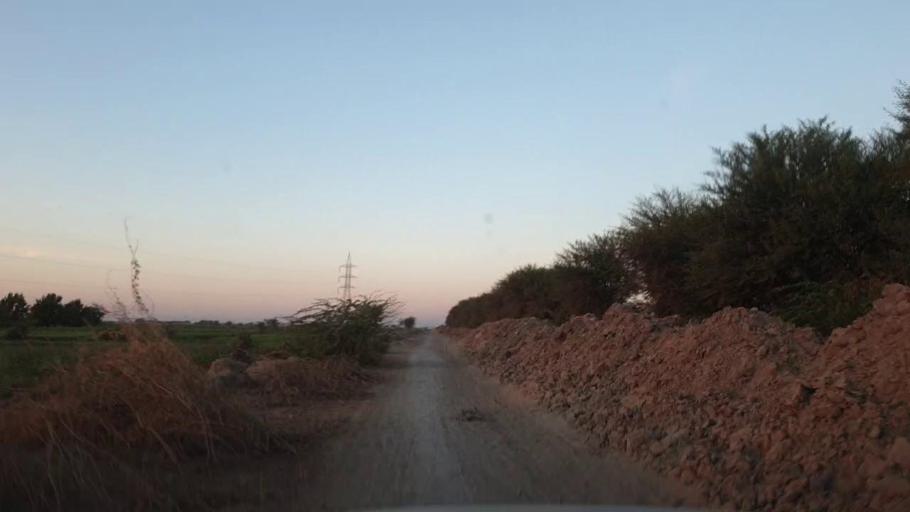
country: PK
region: Sindh
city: Kunri
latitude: 25.1513
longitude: 69.4467
